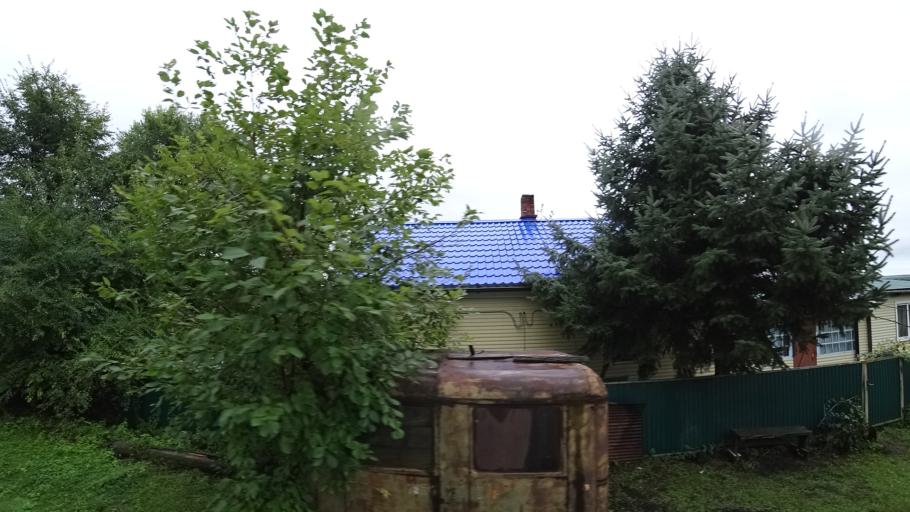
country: RU
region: Primorskiy
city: Monastyrishche
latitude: 44.2585
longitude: 132.4114
